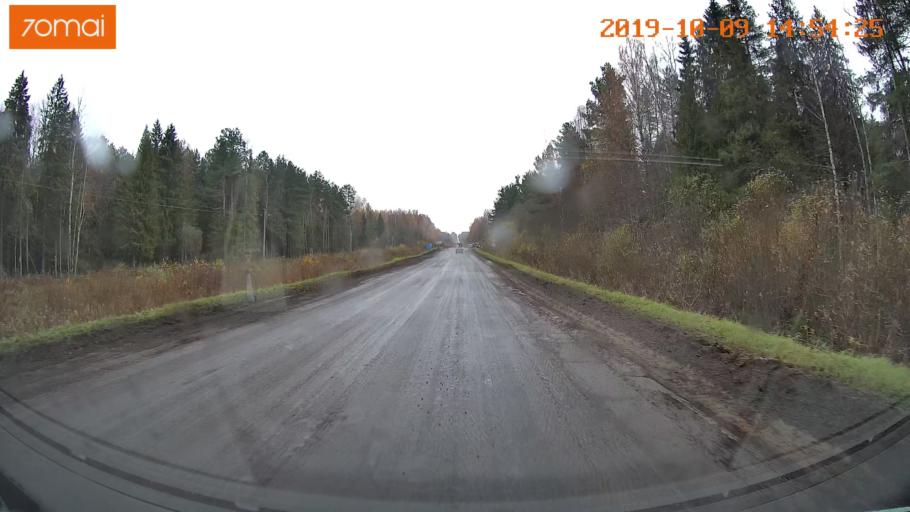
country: RU
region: Kostroma
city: Chistyye Bory
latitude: 58.3569
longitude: 41.6427
